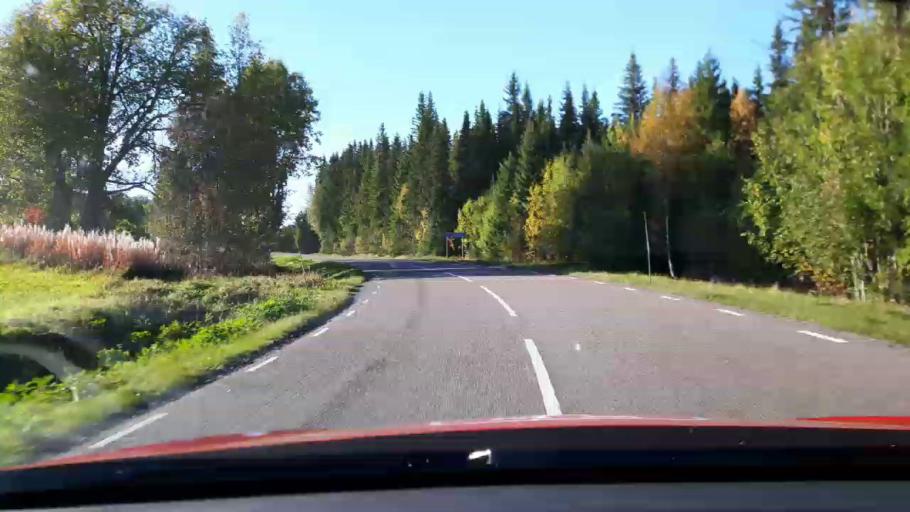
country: SE
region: Jaemtland
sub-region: Stroemsunds Kommun
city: Stroemsund
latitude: 63.8434
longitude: 15.3483
